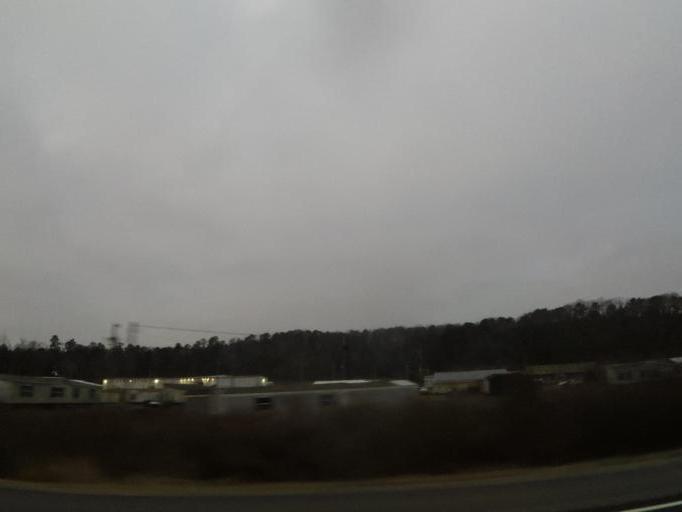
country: US
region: Alabama
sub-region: Cullman County
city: Cullman
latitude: 34.1761
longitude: -86.8764
